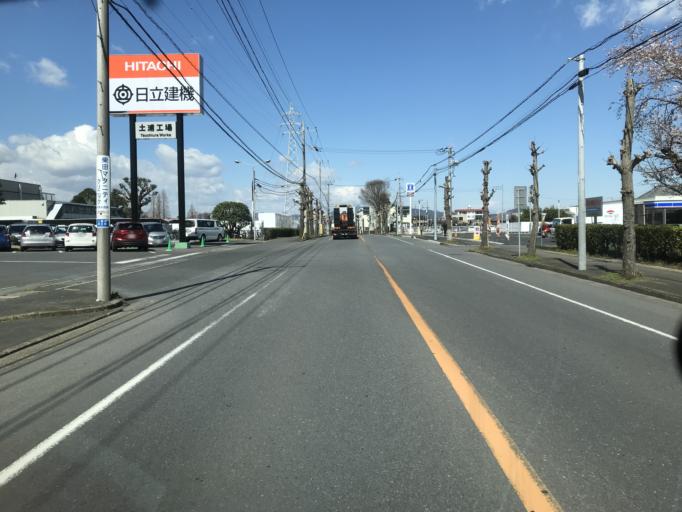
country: JP
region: Ibaraki
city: Ishioka
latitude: 36.1137
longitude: 140.2474
